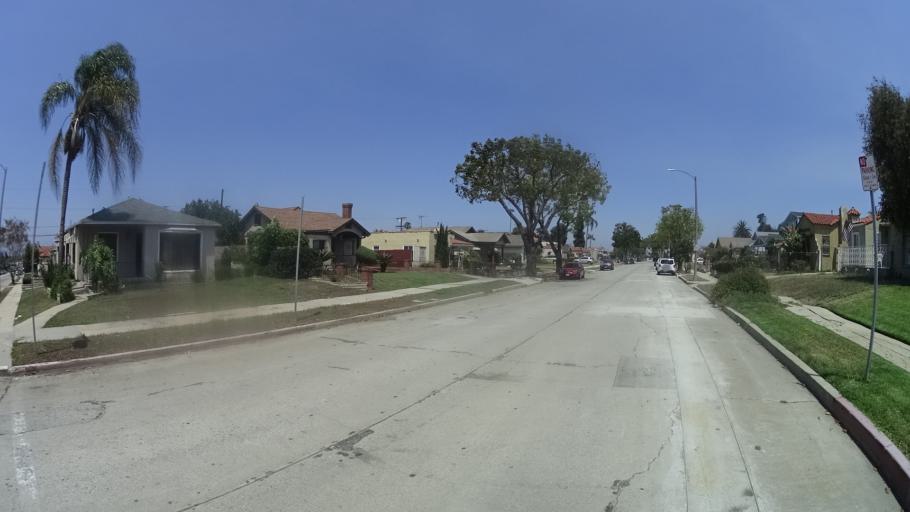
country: US
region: California
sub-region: Los Angeles County
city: Inglewood
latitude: 33.9718
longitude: -118.3242
